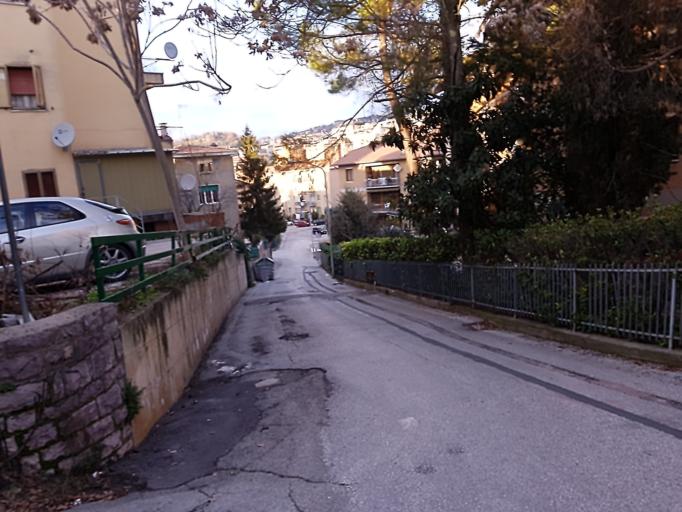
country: IT
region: Umbria
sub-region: Provincia di Perugia
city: Perugia
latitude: 43.0996
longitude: 12.3784
